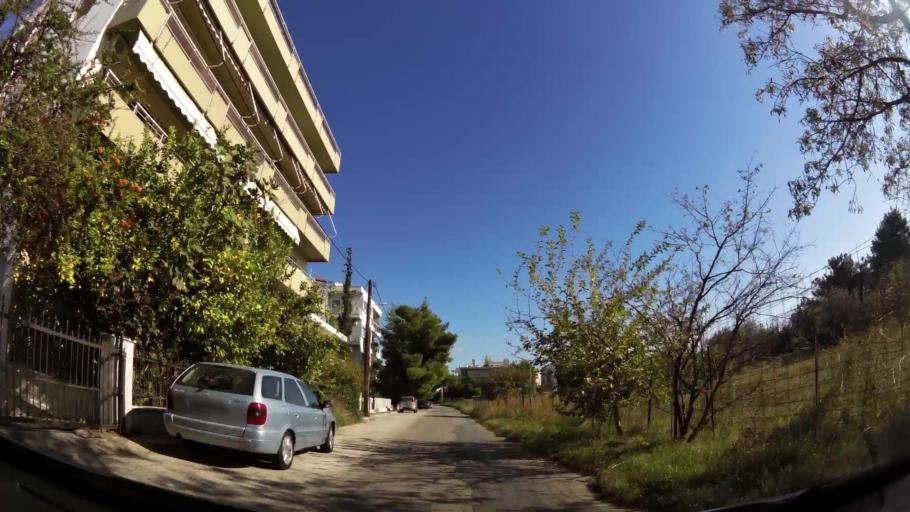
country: GR
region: Attica
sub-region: Nomarchia Athinas
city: Lykovrysi
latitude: 38.0610
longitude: 23.7822
